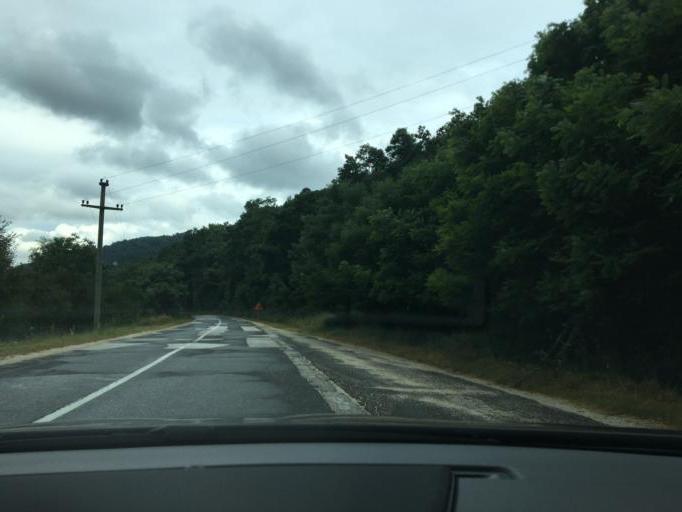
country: MK
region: Kriva Palanka
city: Kriva Palanka
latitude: 42.2239
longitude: 22.4203
